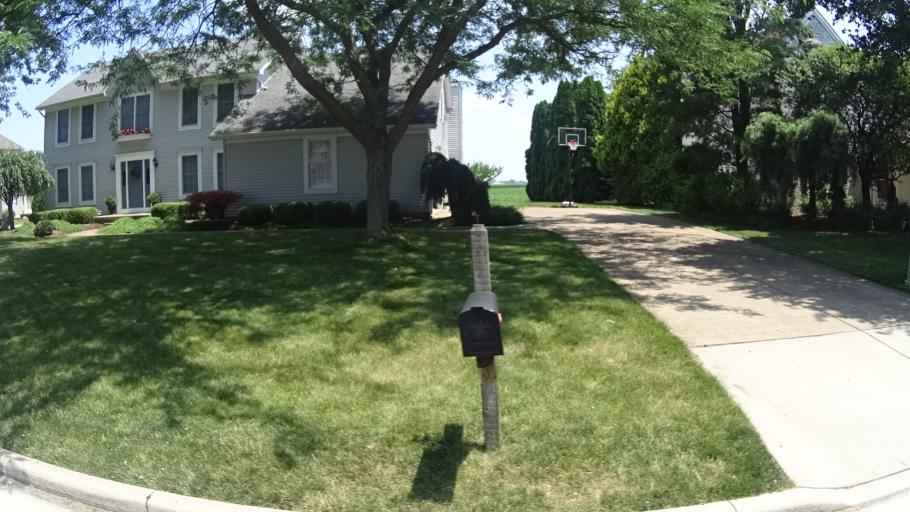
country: US
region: Ohio
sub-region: Erie County
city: Huron
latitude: 41.4072
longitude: -82.6342
